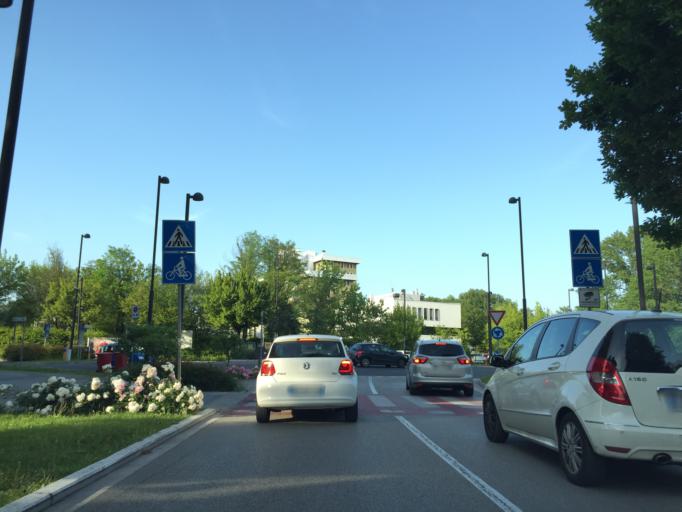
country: IT
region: Friuli Venezia Giulia
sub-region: Provincia di Pordenone
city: Pordenone
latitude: 45.9557
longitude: 12.6651
